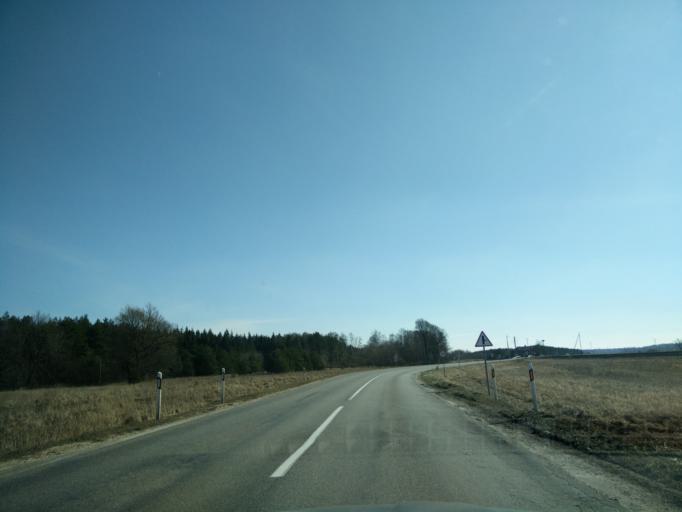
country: LT
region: Klaipedos apskritis
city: Silute
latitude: 55.3284
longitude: 21.5216
